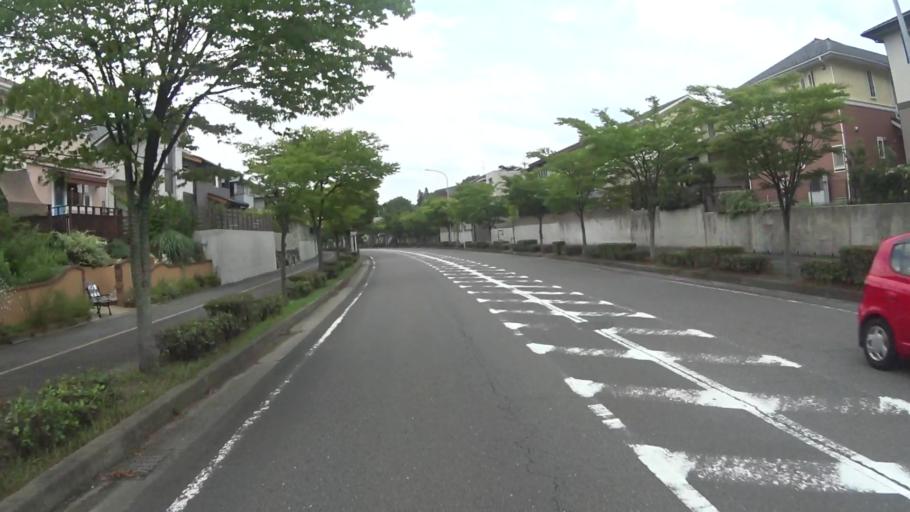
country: JP
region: Nara
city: Nara-shi
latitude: 34.7248
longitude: 135.7767
